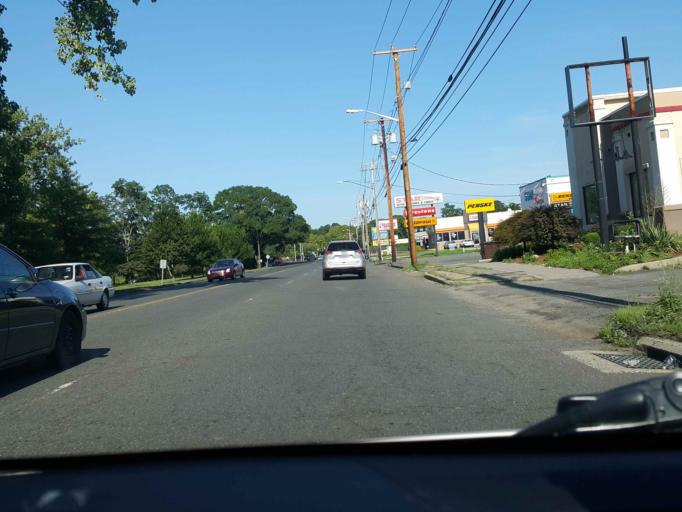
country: US
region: Connecticut
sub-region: New Haven County
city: West Haven
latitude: 41.2970
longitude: -72.9531
